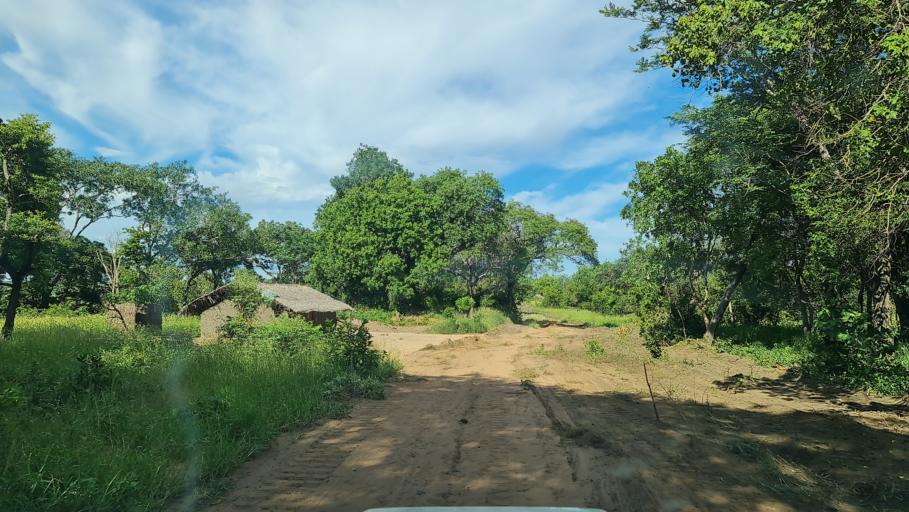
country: MZ
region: Nampula
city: Ilha de Mocambique
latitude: -15.5066
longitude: 40.1471
